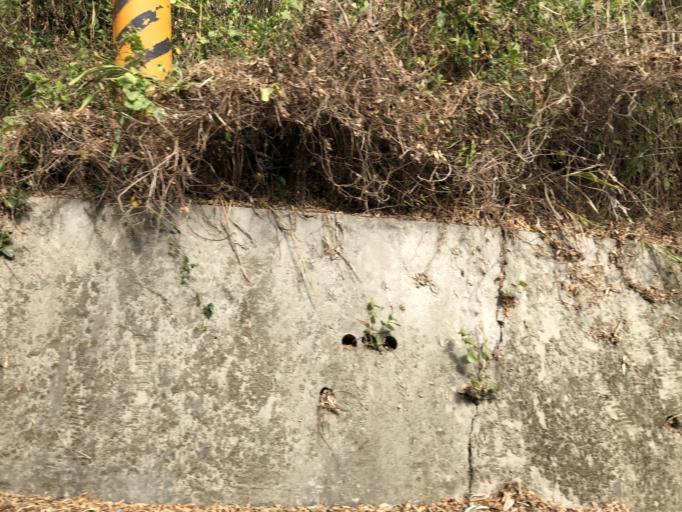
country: TW
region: Taiwan
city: Yujing
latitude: 23.0276
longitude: 120.3943
